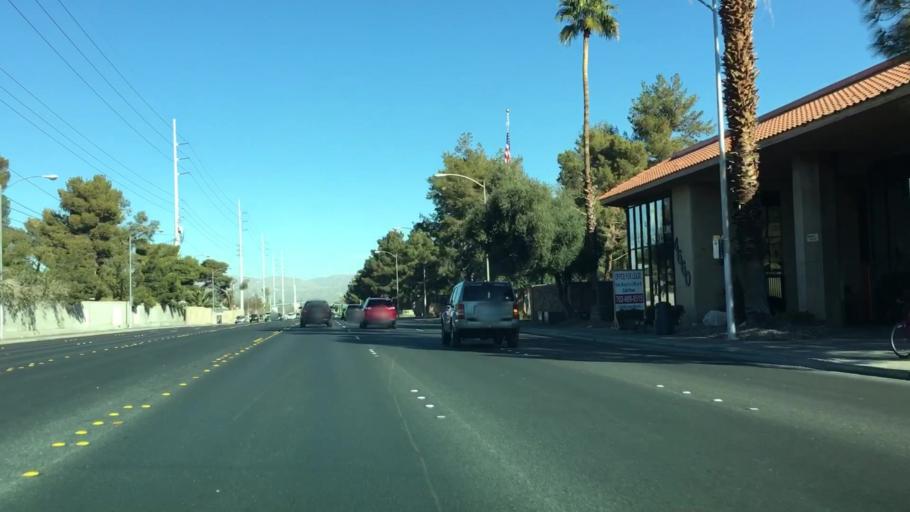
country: US
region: Nevada
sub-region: Clark County
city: Winchester
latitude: 36.1042
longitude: -115.1190
